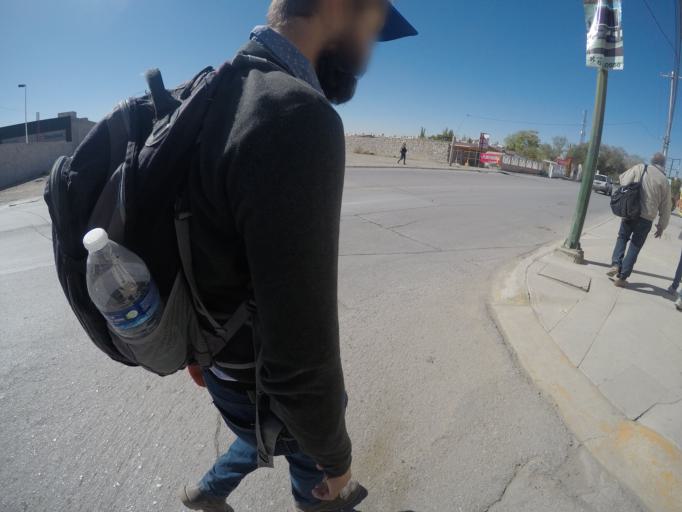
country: US
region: Texas
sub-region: El Paso County
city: Socorro
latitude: 31.6921
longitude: -106.3627
